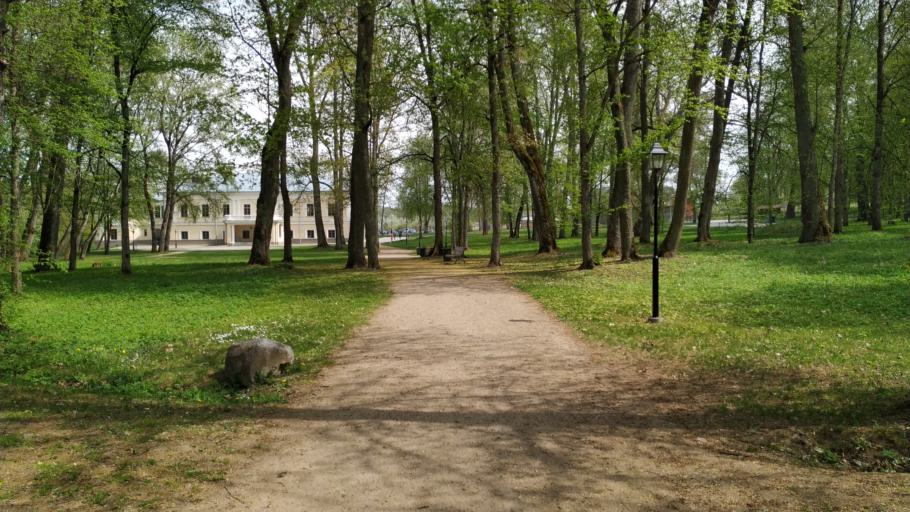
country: LT
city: Salcininkai
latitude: 54.4335
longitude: 25.2963
